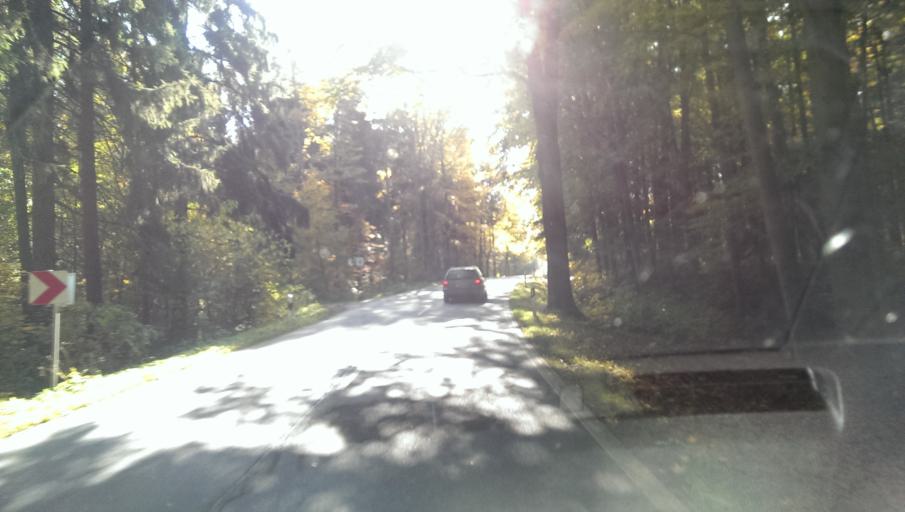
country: DE
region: Saxony
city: Dohma
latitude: 50.8487
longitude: 13.9610
